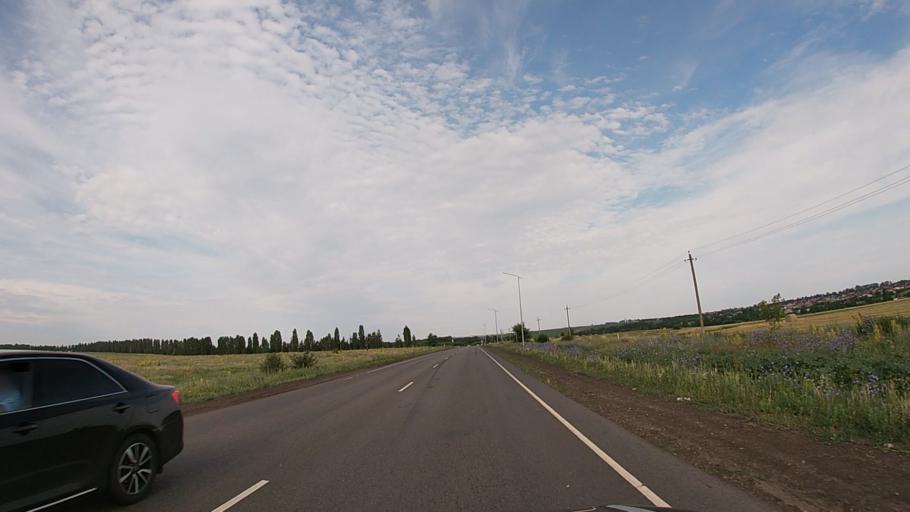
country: RU
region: Belgorod
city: Severnyy
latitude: 50.6656
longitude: 36.5339
